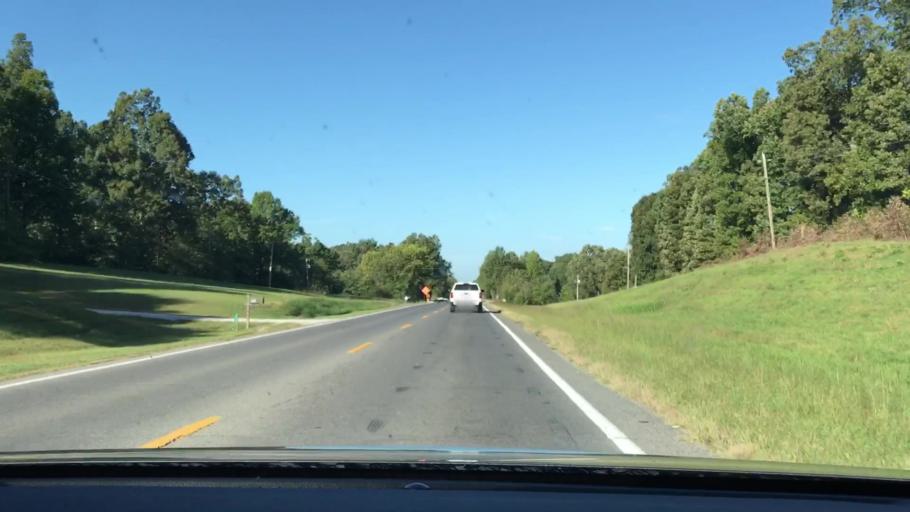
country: US
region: Kentucky
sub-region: Marshall County
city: Calvert City
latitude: 37.0043
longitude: -88.3607
